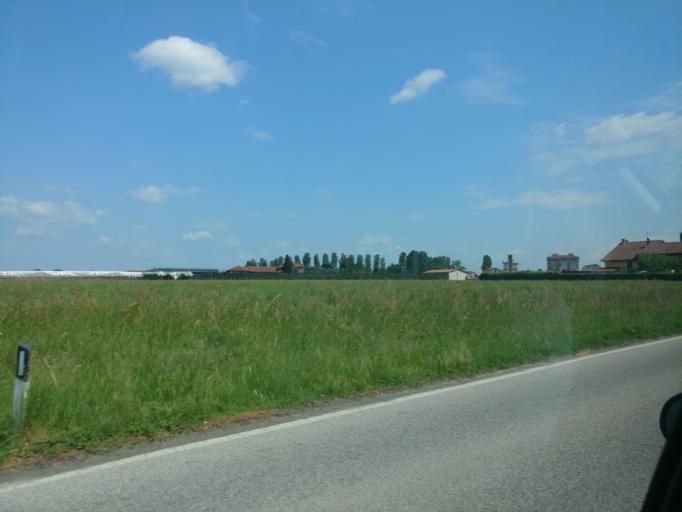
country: IT
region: Piedmont
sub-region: Provincia di Cuneo
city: Saluzzo
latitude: 44.6553
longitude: 7.4880
